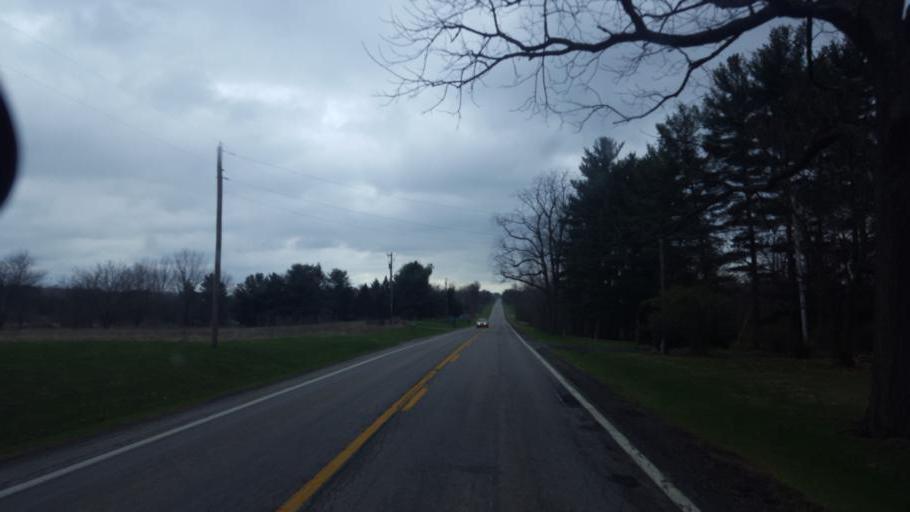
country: US
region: Ohio
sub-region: Morrow County
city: Cardington
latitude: 40.4015
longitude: -82.8440
